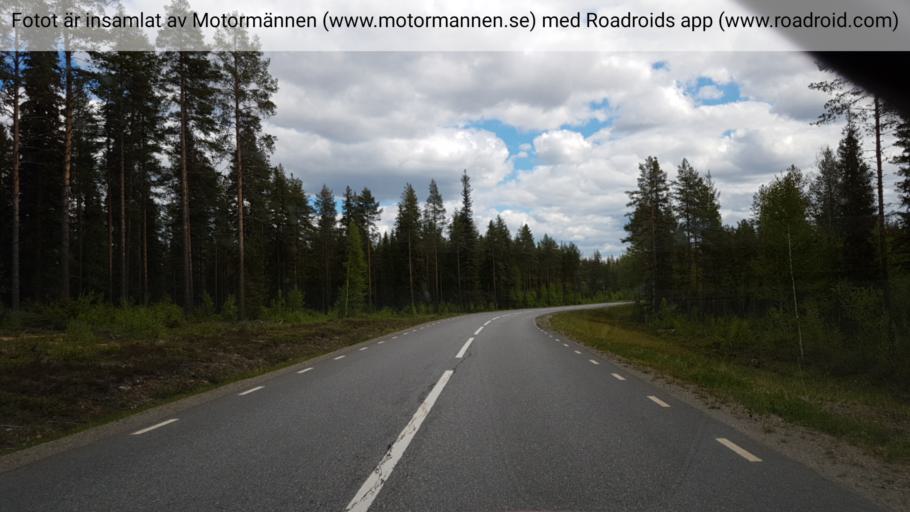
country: SE
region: Vaesterbotten
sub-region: Skelleftea Kommun
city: Langsele
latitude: 64.8377
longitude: 19.8909
